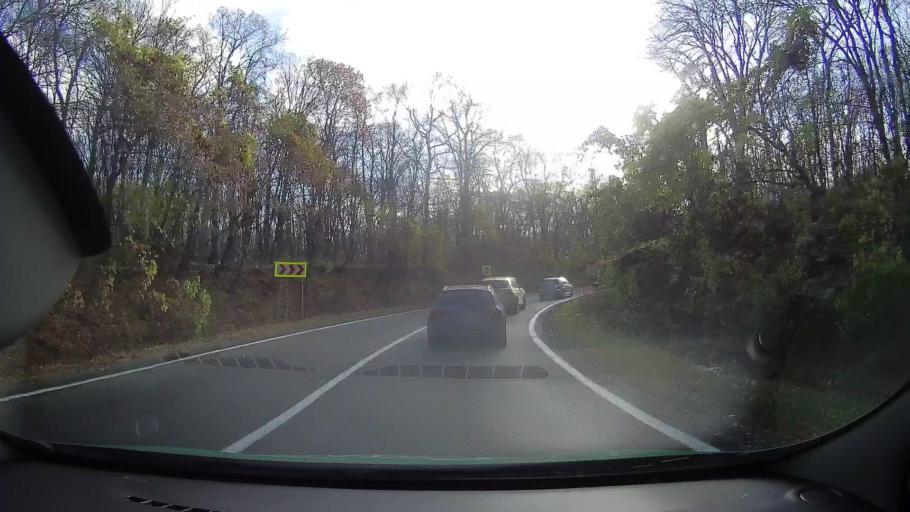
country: RO
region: Tulcea
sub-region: Comuna Topolog
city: Topolog
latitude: 44.9082
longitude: 28.4185
